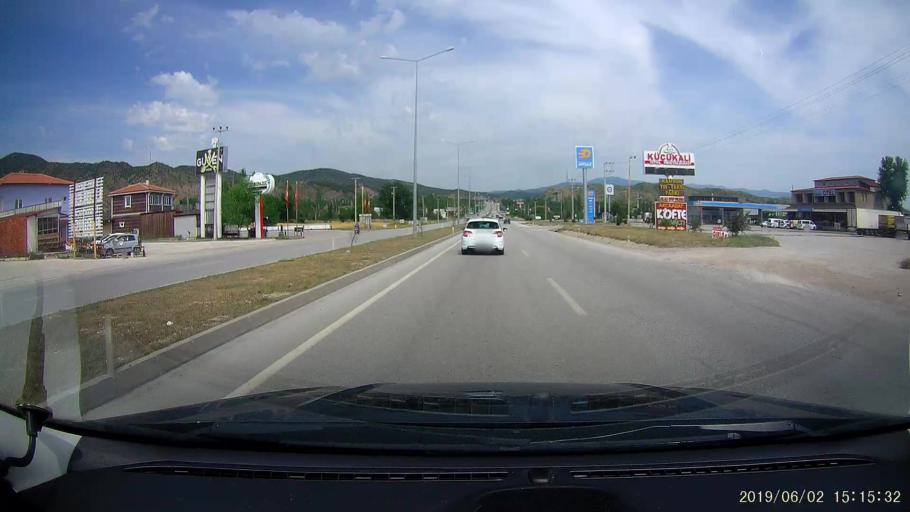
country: TR
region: Corum
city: Osmancik
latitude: 40.9704
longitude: 34.8505
